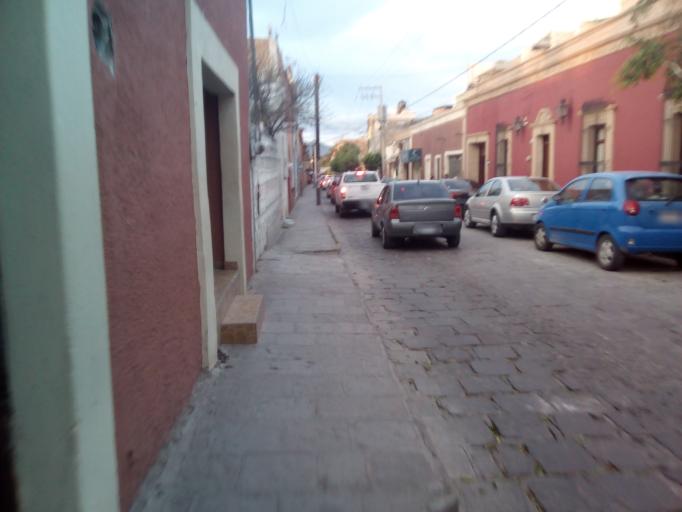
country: MX
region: Guerrero
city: San Luis de la Paz
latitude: 21.2959
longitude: -100.5151
